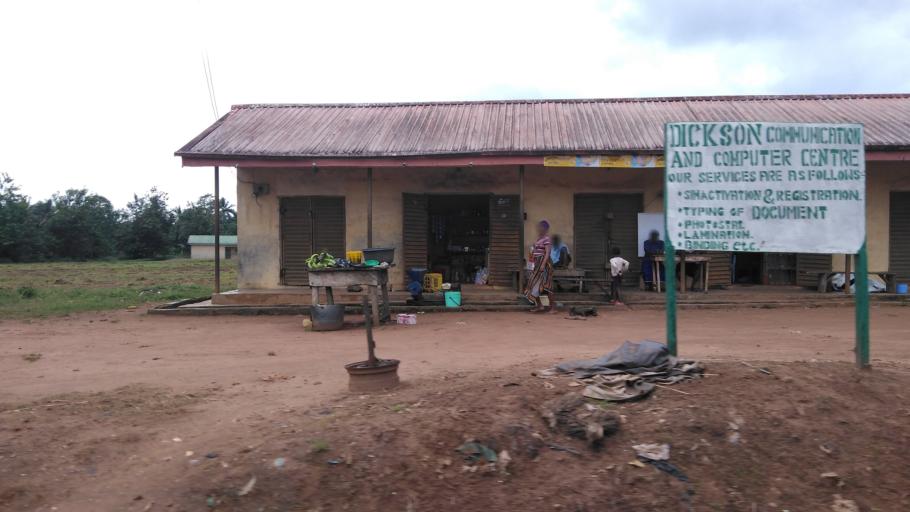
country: NG
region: Ogun
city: Abigi
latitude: 6.5979
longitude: 4.4942
